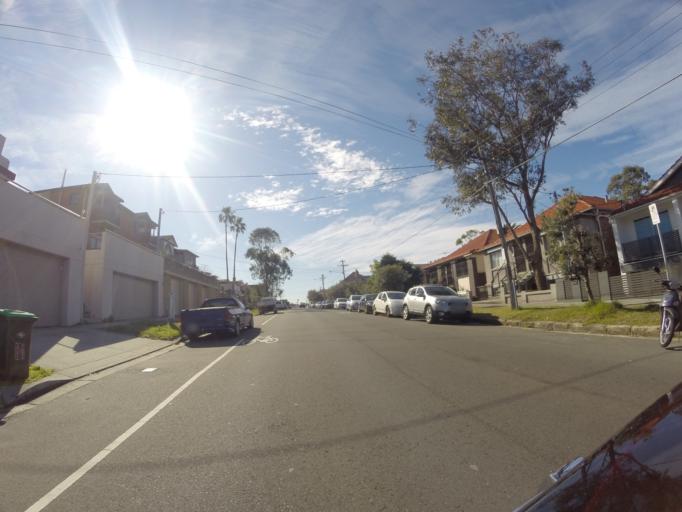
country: AU
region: New South Wales
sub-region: Randwick
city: Coogee
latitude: -33.9252
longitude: 151.2509
